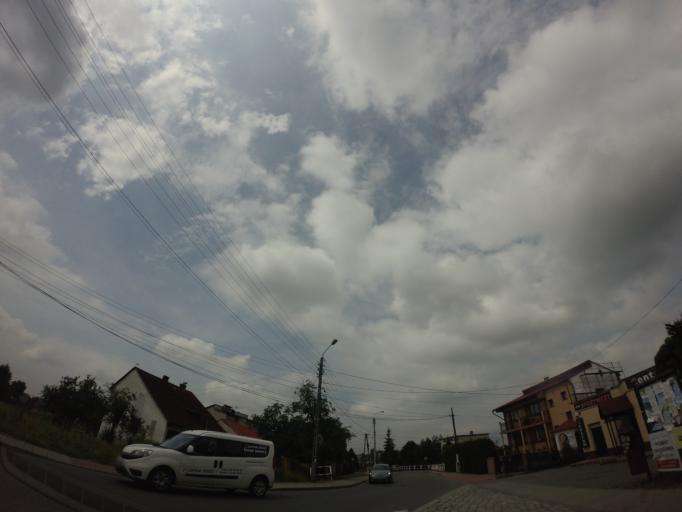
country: PL
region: Lesser Poland Voivodeship
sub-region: Powiat oswiecimski
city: Chelmek
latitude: 50.0740
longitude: 19.2348
